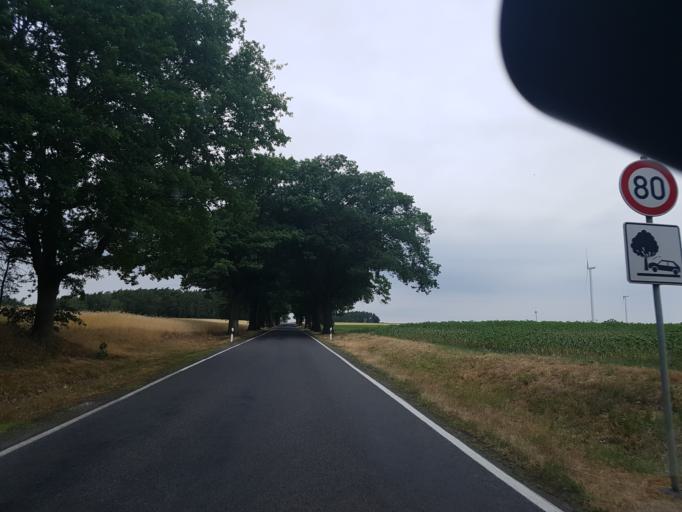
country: DE
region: Brandenburg
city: Hohenbucko
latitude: 51.6956
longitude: 13.5059
